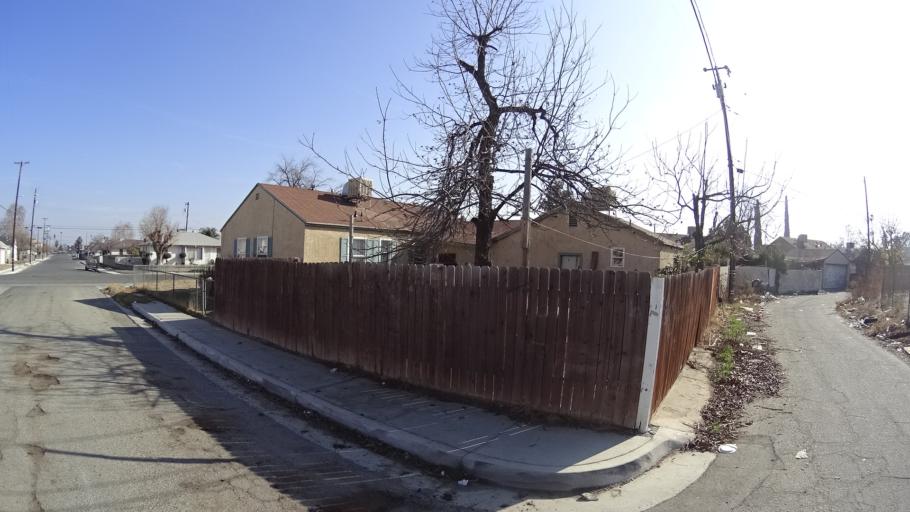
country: US
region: California
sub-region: Kern County
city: Bakersfield
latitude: 35.3589
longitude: -119.0074
